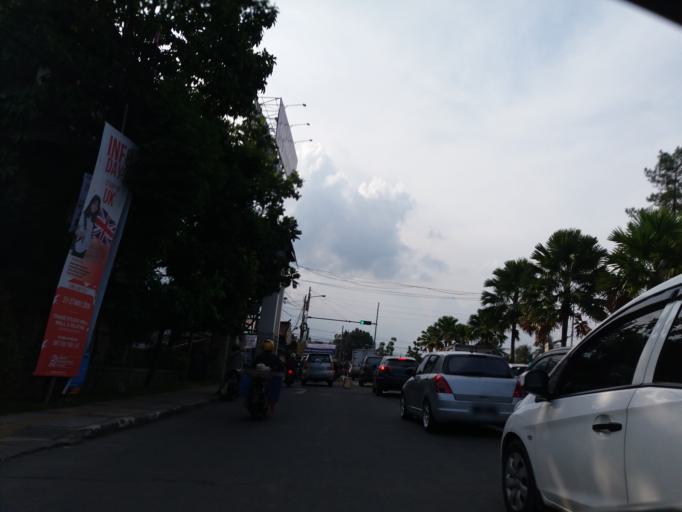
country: ID
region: West Java
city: Bandung
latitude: -6.9502
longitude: 107.6260
